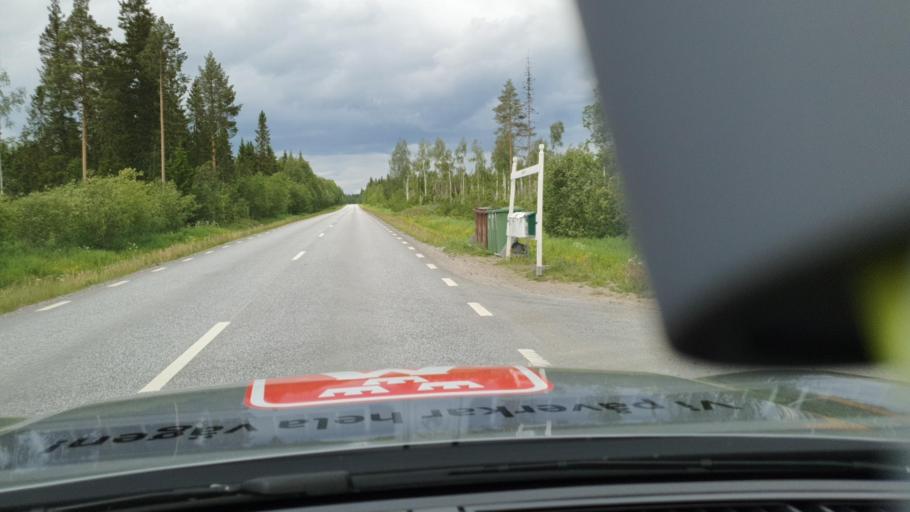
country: SE
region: Norrbotten
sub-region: Lulea Kommun
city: Lulea
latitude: 65.6735
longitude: 22.2226
